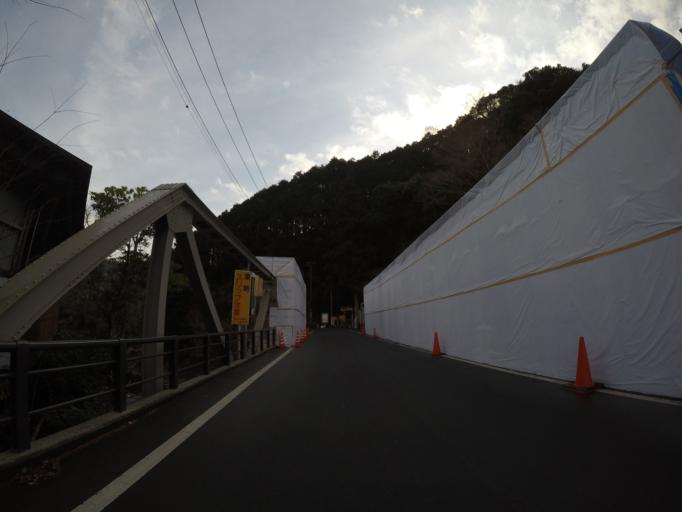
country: JP
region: Shizuoka
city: Heda
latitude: 34.8900
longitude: 138.9247
